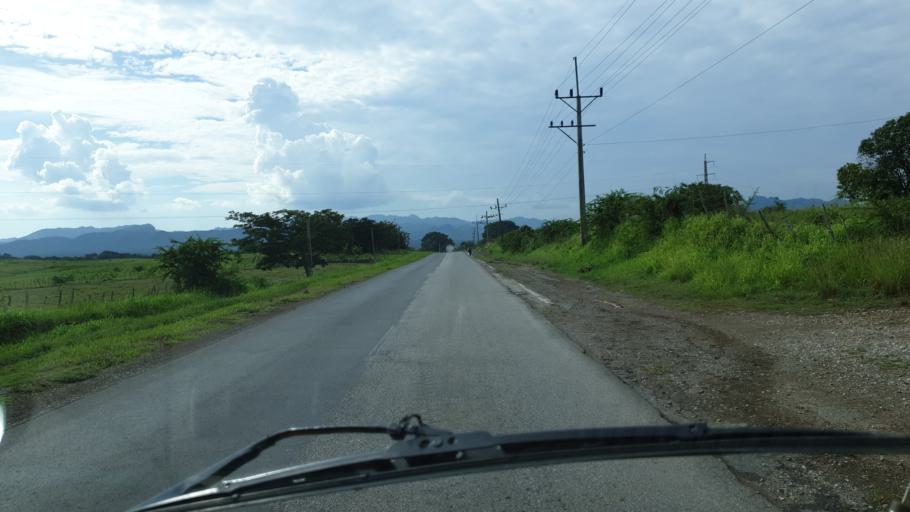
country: CU
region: Cienfuegos
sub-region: Municipio de Cienfuegos
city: Cumanayagua
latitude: 22.0726
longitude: -80.3077
